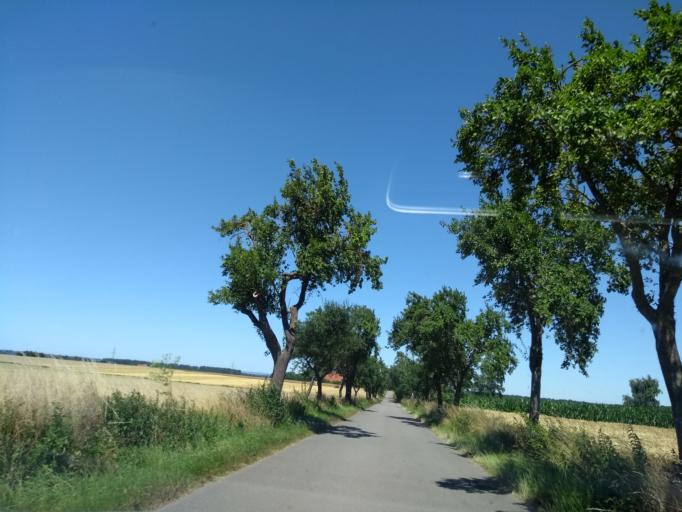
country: DE
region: North Rhine-Westphalia
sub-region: Regierungsbezirk Detmold
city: Salzkotten
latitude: 51.6532
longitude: 8.6383
